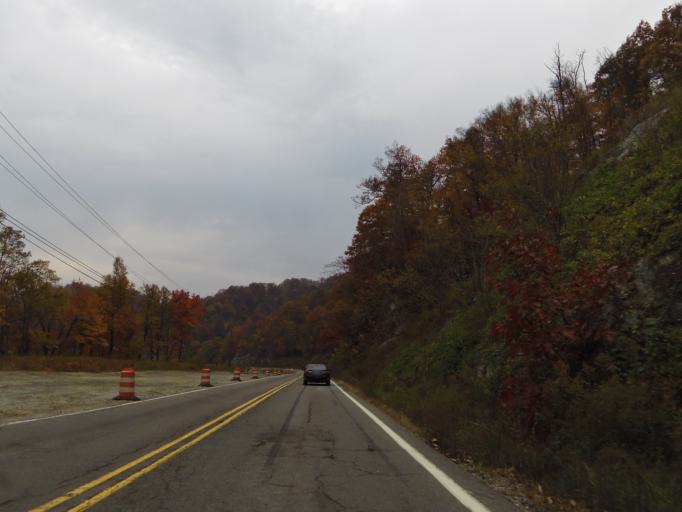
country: US
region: North Carolina
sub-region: Watauga County
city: Blowing Rock
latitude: 36.1145
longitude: -81.6543
